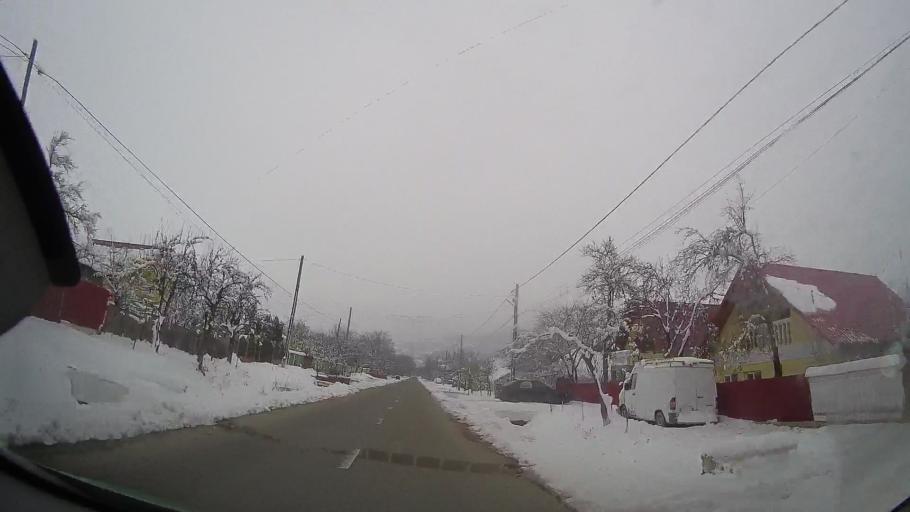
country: RO
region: Vaslui
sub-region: Comuna Bacesti
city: Bacesti
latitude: 46.8226
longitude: 27.2014
